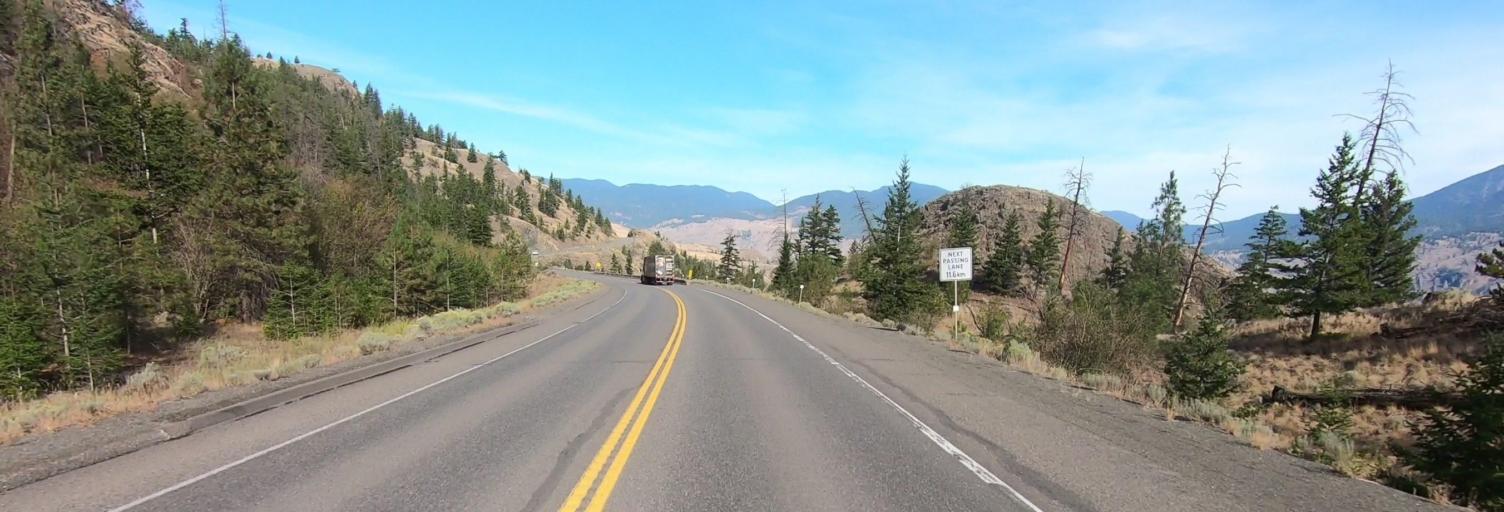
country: CA
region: British Columbia
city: Logan Lake
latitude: 50.7528
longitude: -120.7295
